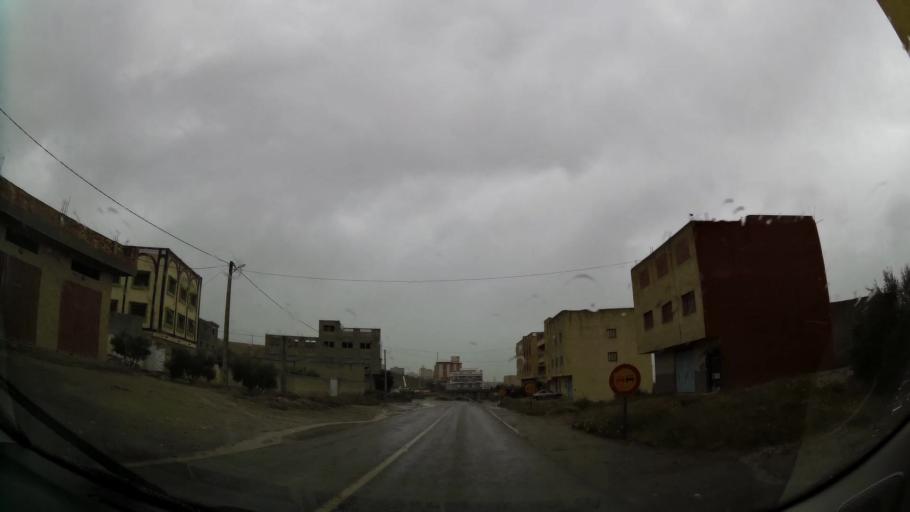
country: MA
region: Oriental
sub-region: Nador
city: Midar
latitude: 34.8902
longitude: -3.7357
